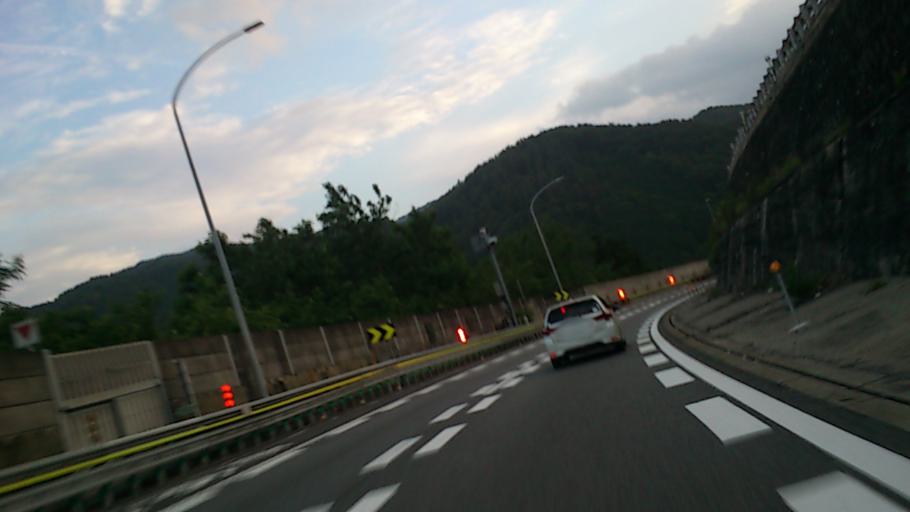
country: JP
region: Nagano
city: Iida
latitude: 35.4461
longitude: 137.7436
